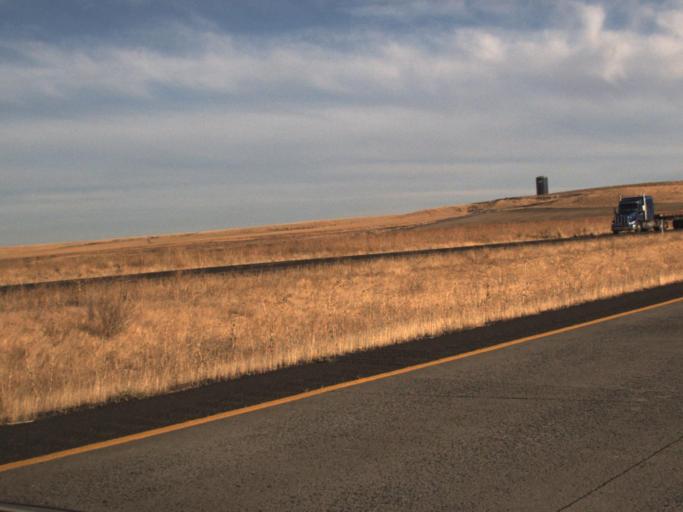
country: US
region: Washington
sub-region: Franklin County
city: Connell
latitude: 46.6789
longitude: -118.8431
